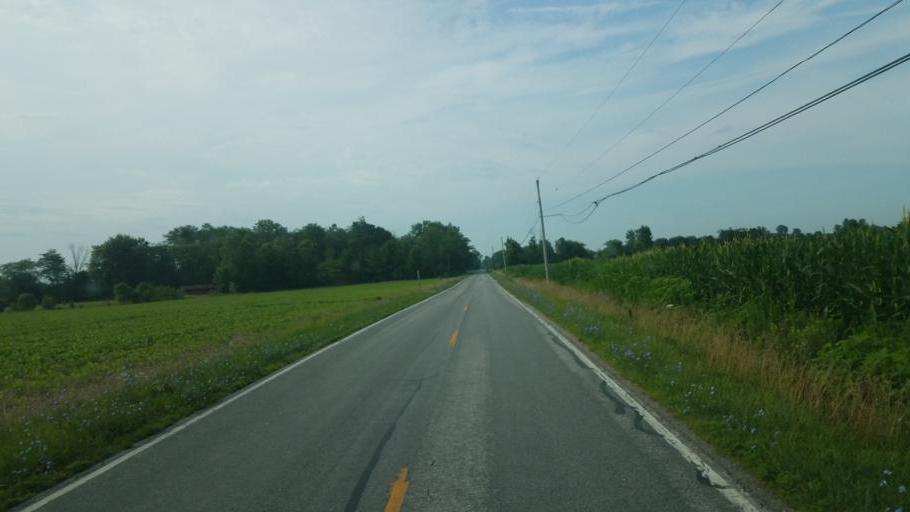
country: US
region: Ohio
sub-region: Union County
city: New California
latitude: 40.2095
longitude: -83.1666
